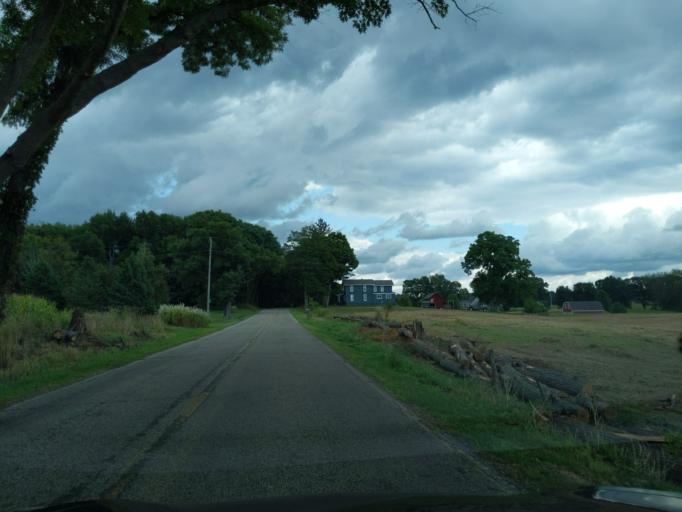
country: US
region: Michigan
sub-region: Eaton County
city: Eaton Rapids
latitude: 42.3784
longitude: -84.6148
